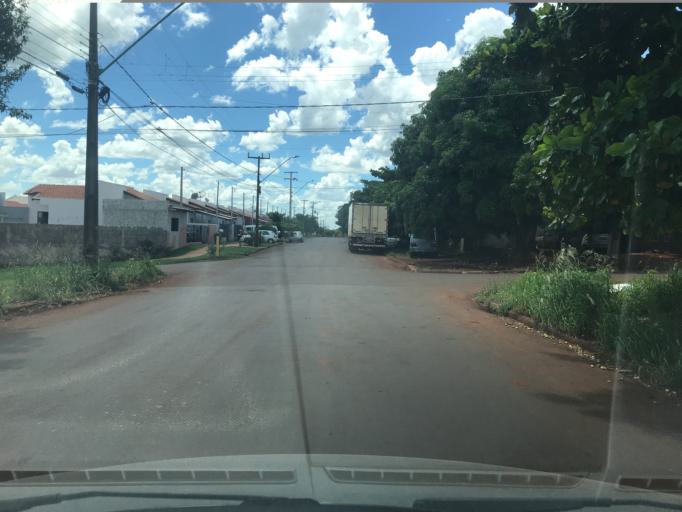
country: BR
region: Parana
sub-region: Palotina
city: Palotina
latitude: -24.2715
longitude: -53.8485
